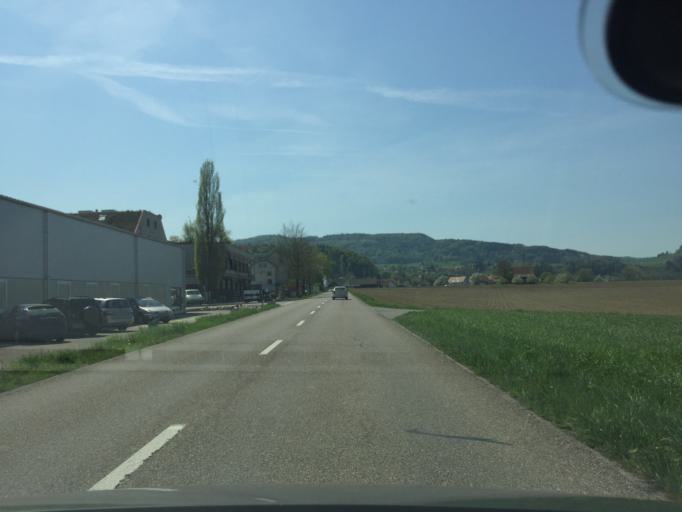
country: CH
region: Zurich
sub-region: Bezirk Buelach
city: Freienstein
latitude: 47.5820
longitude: 8.6147
